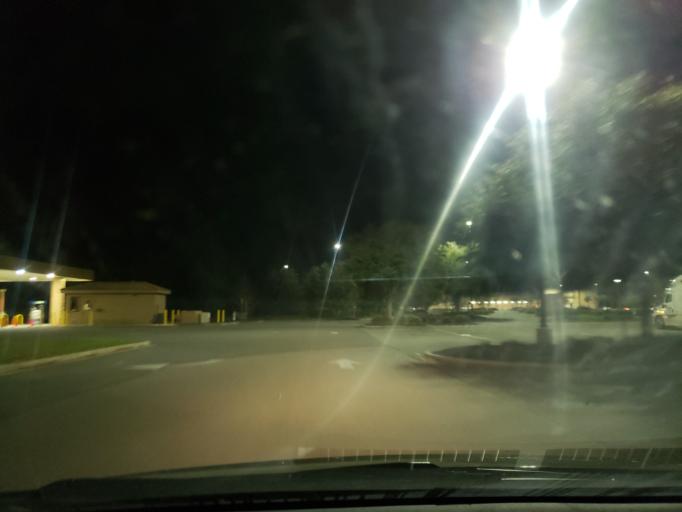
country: US
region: Georgia
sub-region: Chatham County
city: Isle of Hope
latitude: 31.9894
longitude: -81.0796
